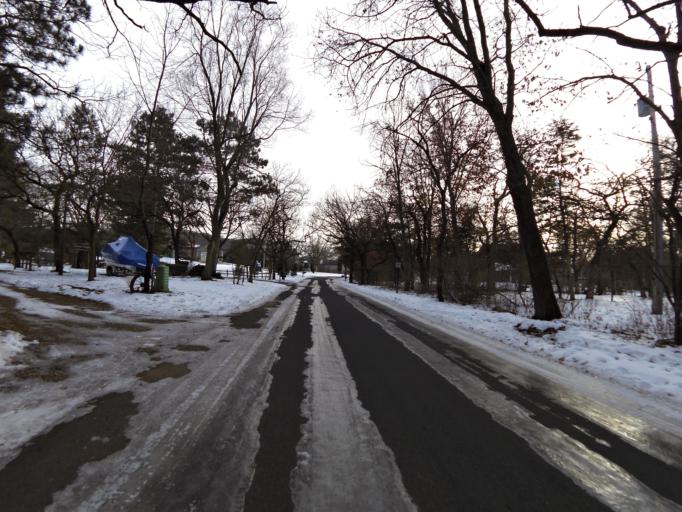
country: US
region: Minnesota
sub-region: Washington County
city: Lake Saint Croix Beach
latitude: 44.9090
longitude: -92.7715
